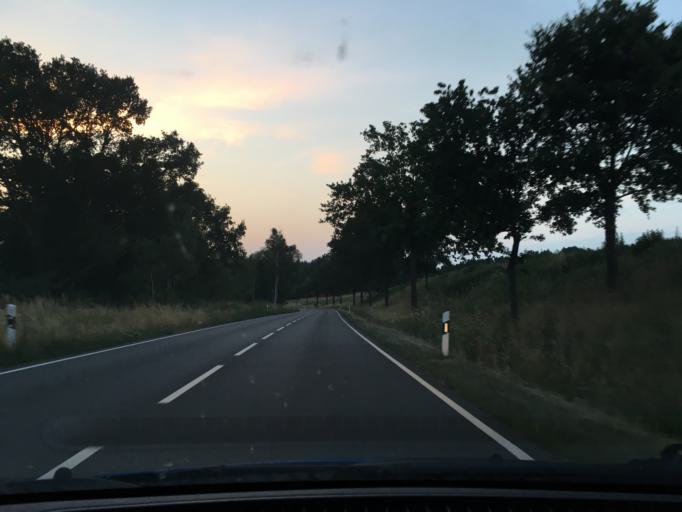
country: DE
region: Lower Saxony
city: Bad Bevensen
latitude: 53.0761
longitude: 10.5613
